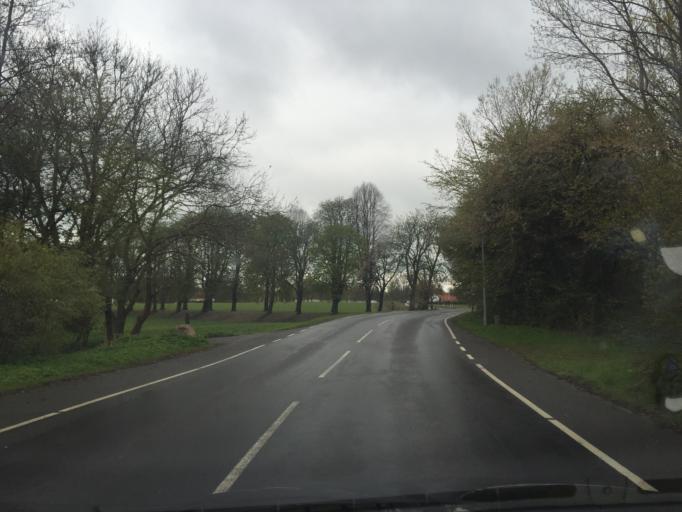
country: DK
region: Capital Region
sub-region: Hoje-Taastrup Kommune
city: Taastrup
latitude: 55.6866
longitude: 12.2458
